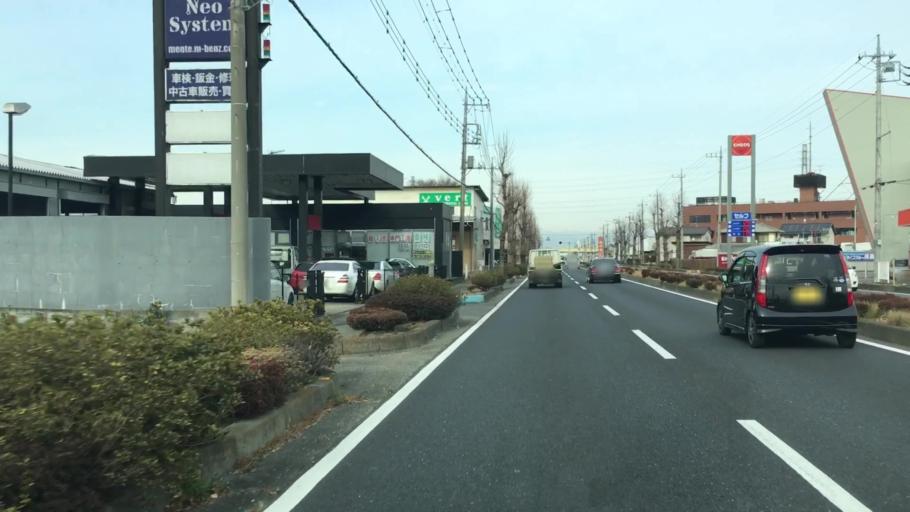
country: JP
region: Saitama
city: Kumagaya
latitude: 36.1658
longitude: 139.3706
